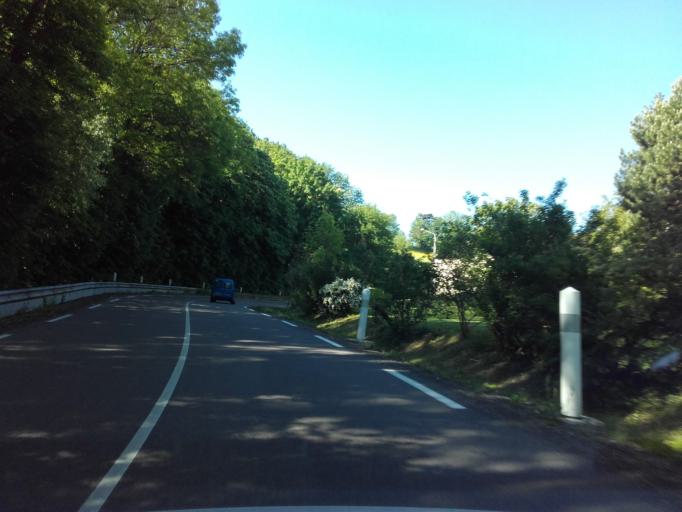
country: FR
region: Bourgogne
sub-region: Departement de la Cote-d'Or
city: Nolay
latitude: 46.9580
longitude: 4.6822
